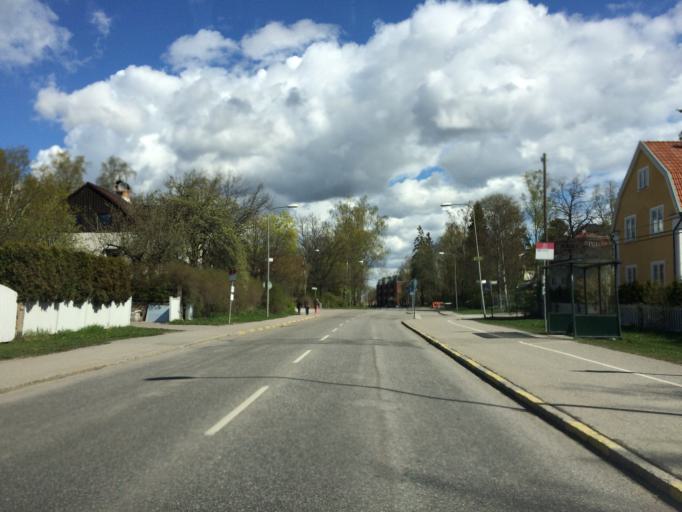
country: SE
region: Stockholm
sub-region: Huddinge Kommun
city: Segeltorp
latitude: 59.2939
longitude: 17.9539
